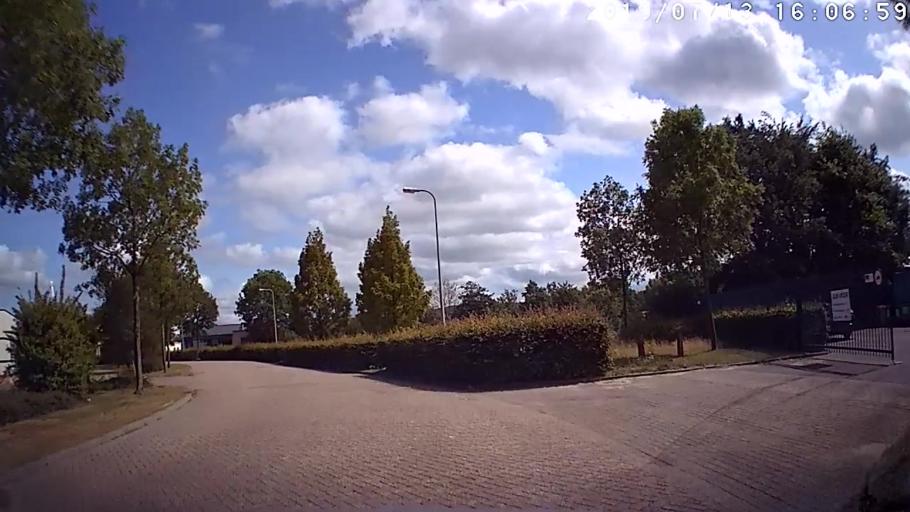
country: NL
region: Overijssel
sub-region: Gemeente Zwolle
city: Zwolle
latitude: 52.4921
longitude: 6.1213
